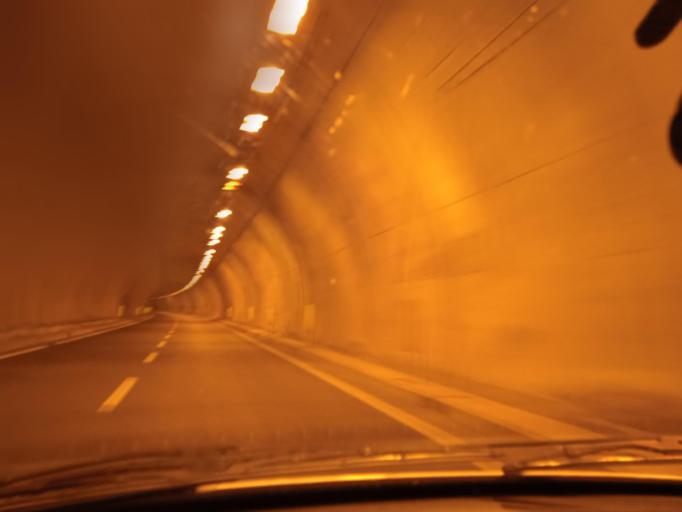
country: IT
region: Sicily
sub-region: Messina
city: Santo Stefano di Camastra
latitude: 38.0046
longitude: 14.3485
